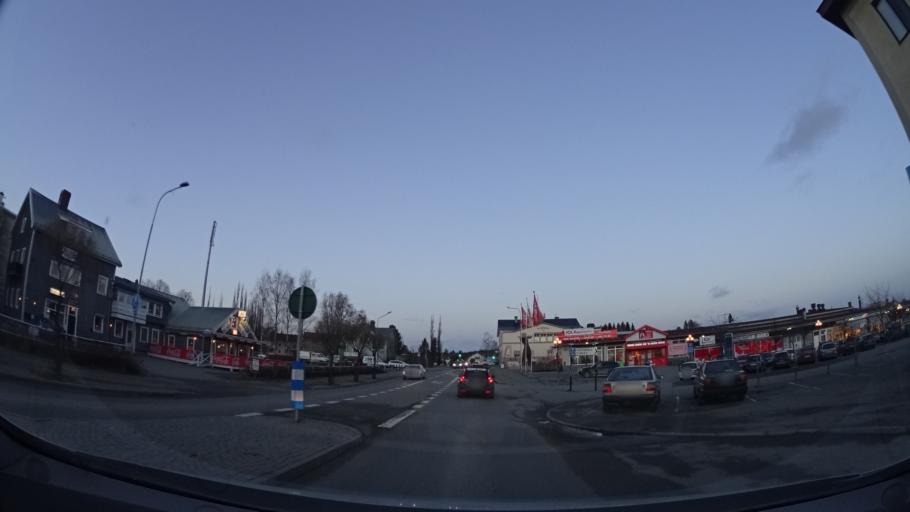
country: SE
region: Jaemtland
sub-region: Stroemsunds Kommun
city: Stroemsund
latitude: 63.8521
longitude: 15.5565
